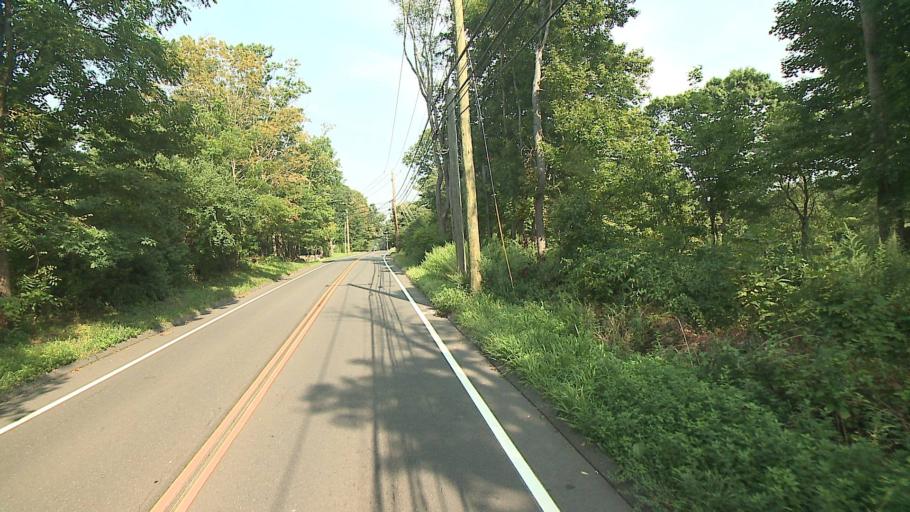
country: US
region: Connecticut
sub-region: Fairfield County
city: Wilton
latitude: 41.2227
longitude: -73.3966
